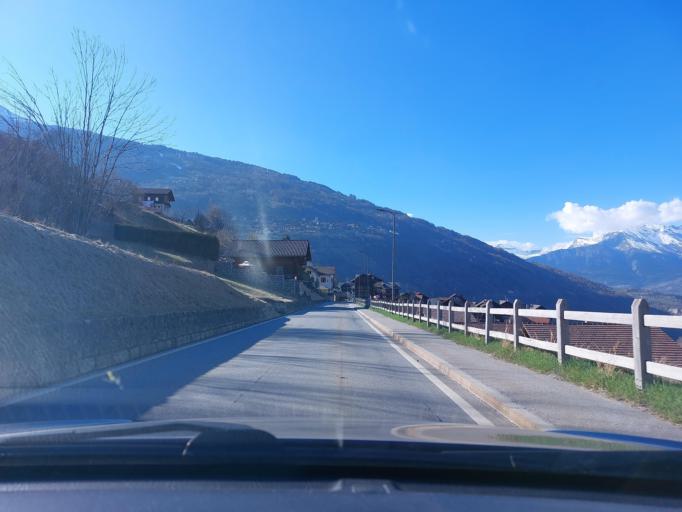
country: CH
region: Valais
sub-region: Herens District
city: Heremence
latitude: 46.1705
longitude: 7.4250
